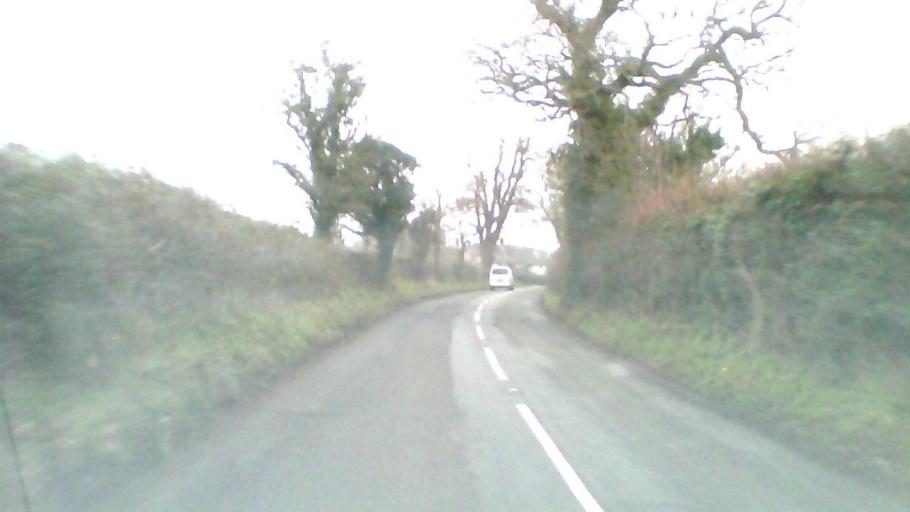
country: GB
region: England
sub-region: Isle of Wight
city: Bembridge
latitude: 50.6821
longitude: -1.0924
